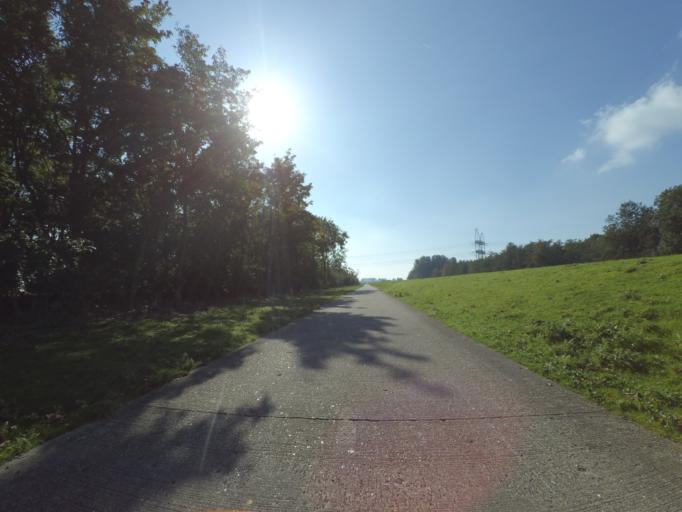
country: NL
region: Gelderland
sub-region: Gemeente Harderwijk
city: Harderwijk
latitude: 52.3784
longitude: 5.6221
